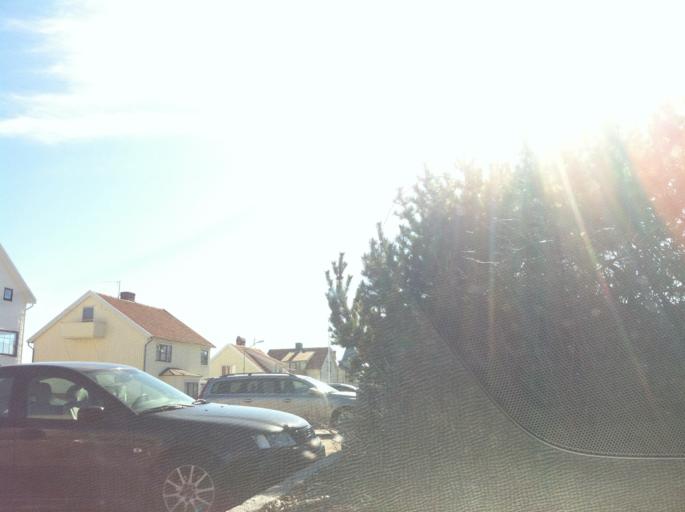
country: SE
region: Vaestra Goetaland
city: Smoegen
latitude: 58.3522
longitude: 11.2217
